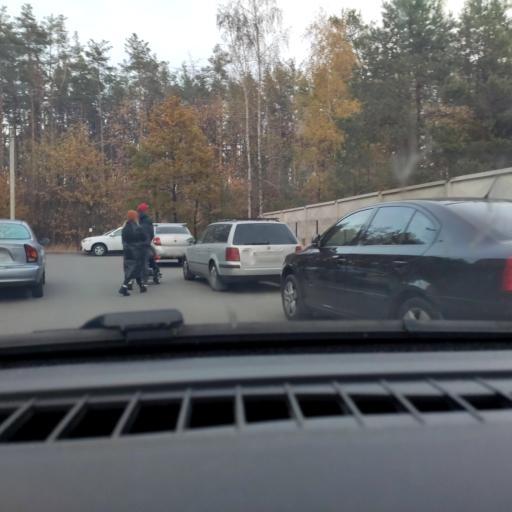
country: RU
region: Voronezj
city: Podgornoye
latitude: 51.7331
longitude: 39.1834
